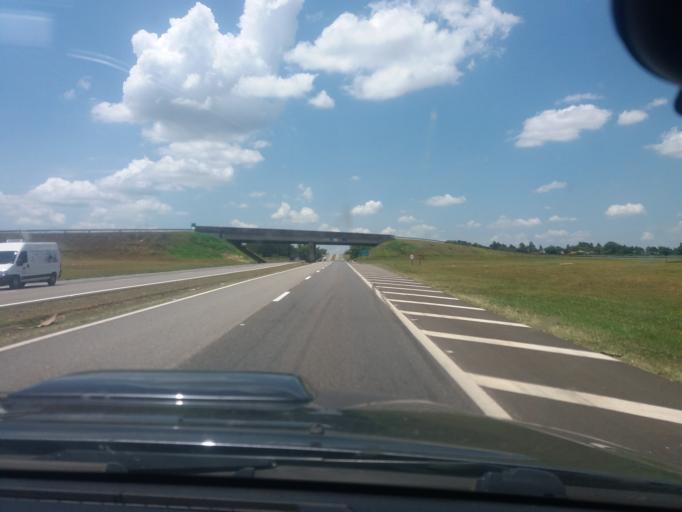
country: BR
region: Sao Paulo
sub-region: Itapetininga
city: Itapetininga
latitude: -23.5686
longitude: -47.9766
